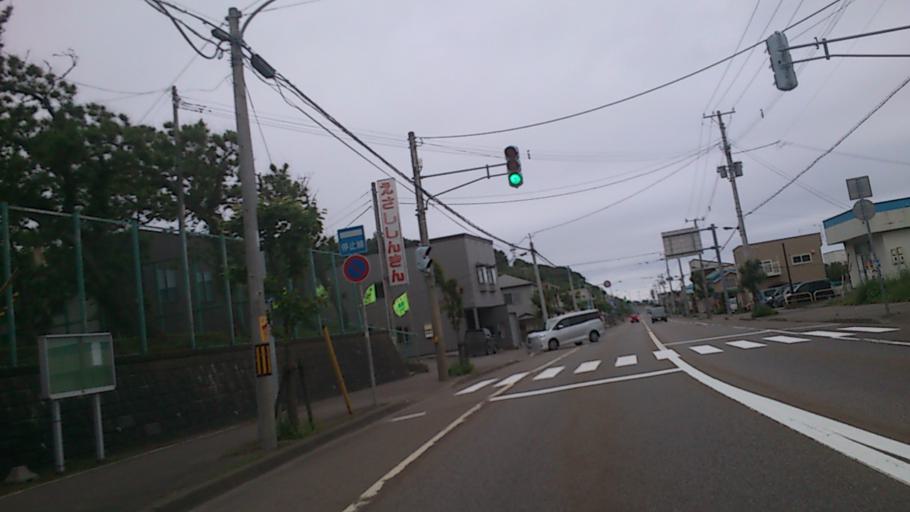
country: JP
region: Hokkaido
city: Kamiiso
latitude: 41.9696
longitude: 140.1373
